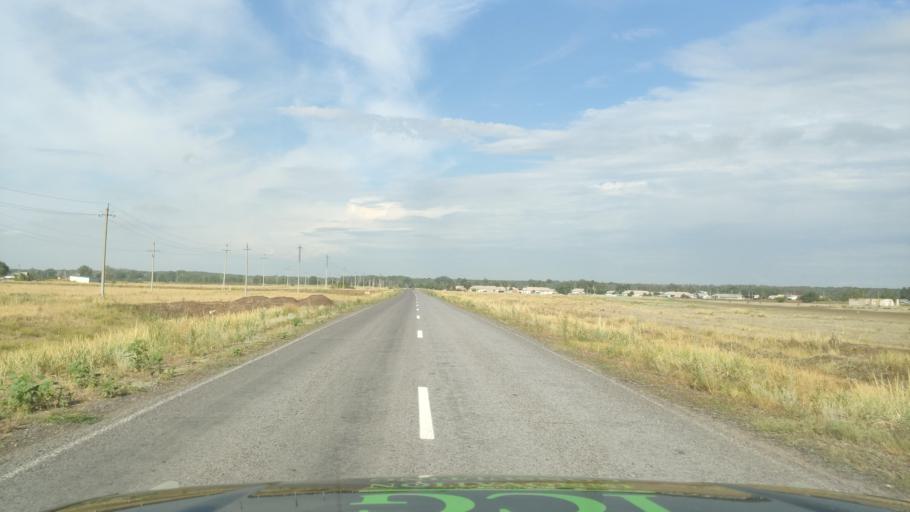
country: KZ
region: Pavlodar
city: Leninskiy
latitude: 52.4777
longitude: 76.8292
